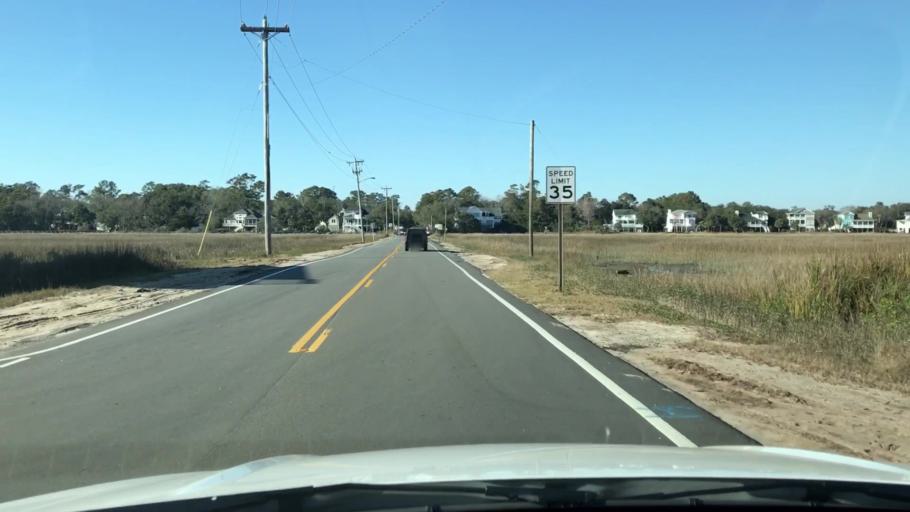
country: US
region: South Carolina
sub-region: Horry County
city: Garden City
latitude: 33.5820
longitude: -78.9964
